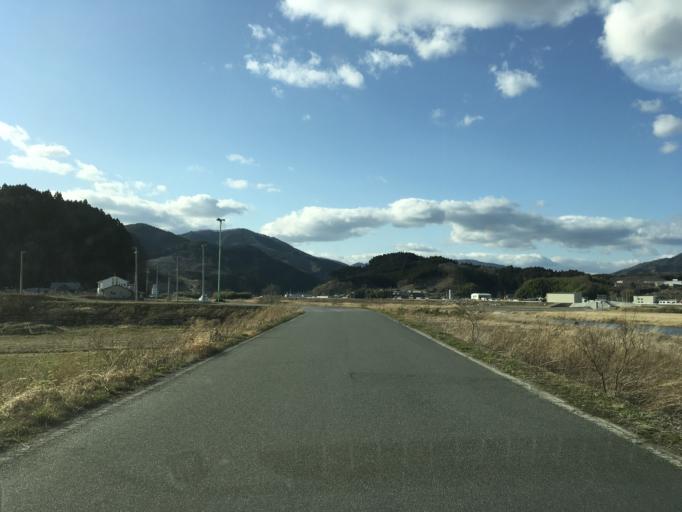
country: JP
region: Iwate
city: Ofunato
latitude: 39.0274
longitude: 141.6125
